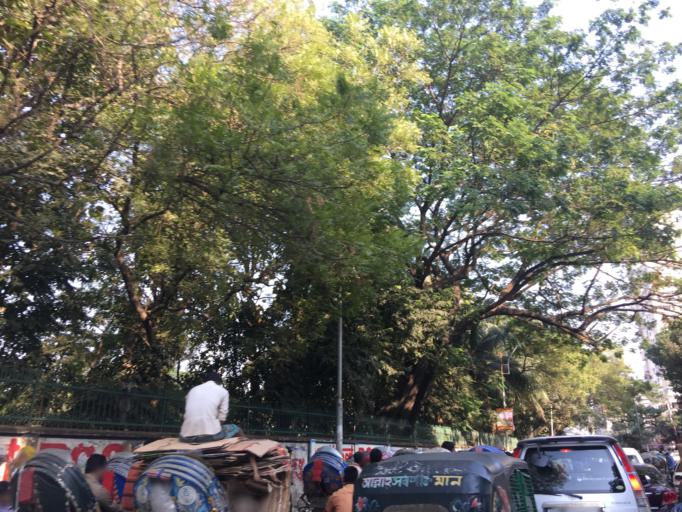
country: BD
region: Dhaka
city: Azimpur
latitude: 23.7249
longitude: 90.3942
